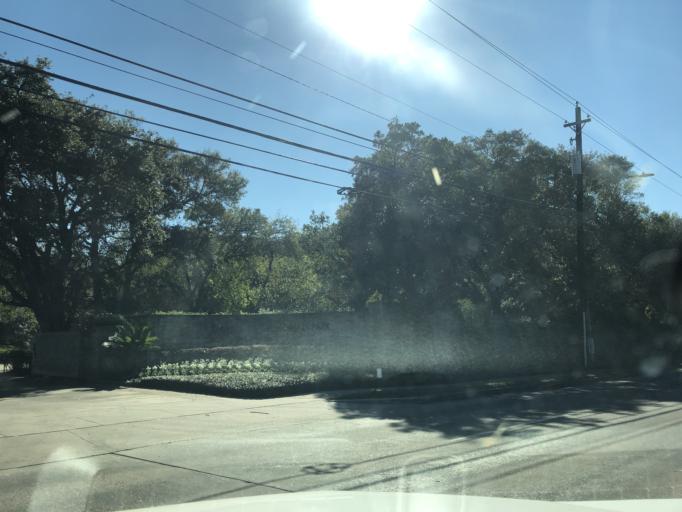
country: US
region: Texas
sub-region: Fort Bend County
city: Missouri City
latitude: 29.6793
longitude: -95.5235
